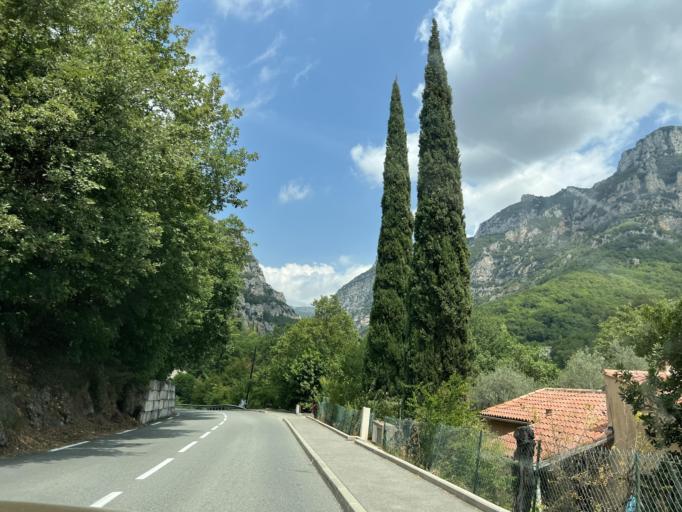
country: FR
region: Provence-Alpes-Cote d'Azur
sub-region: Departement des Alpes-Maritimes
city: Le Rouret
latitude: 43.7172
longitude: 6.9898
